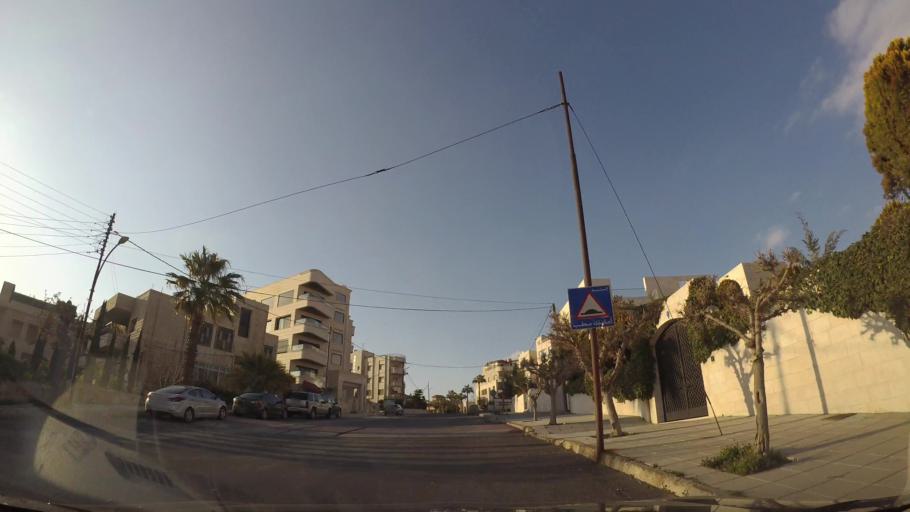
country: JO
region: Amman
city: Al Jubayhah
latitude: 31.9751
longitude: 35.8809
